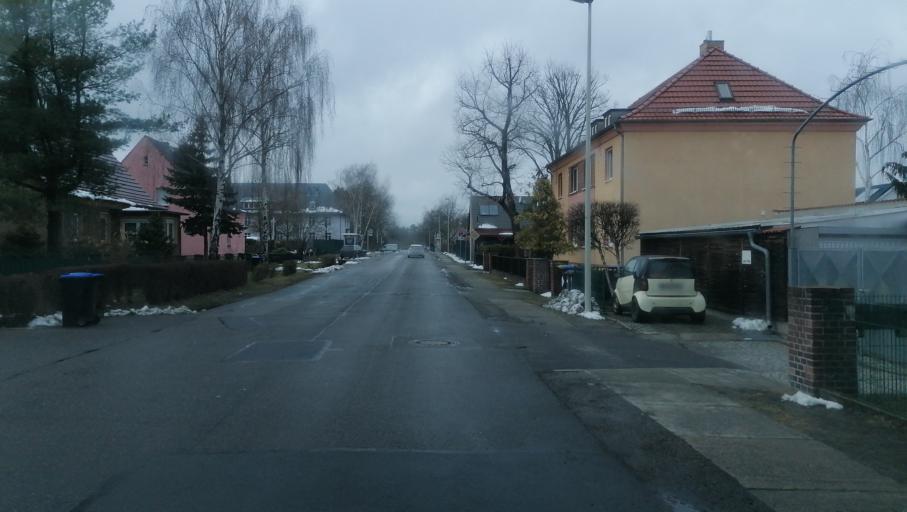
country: DE
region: Brandenburg
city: Cottbus
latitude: 51.7208
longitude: 14.3432
